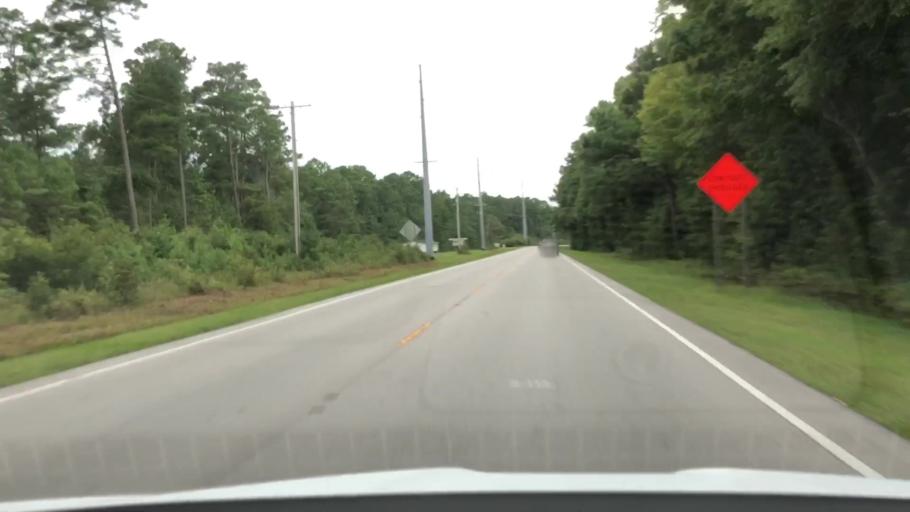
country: US
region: North Carolina
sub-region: Carteret County
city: Cape Carteret
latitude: 34.7461
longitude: -77.0900
